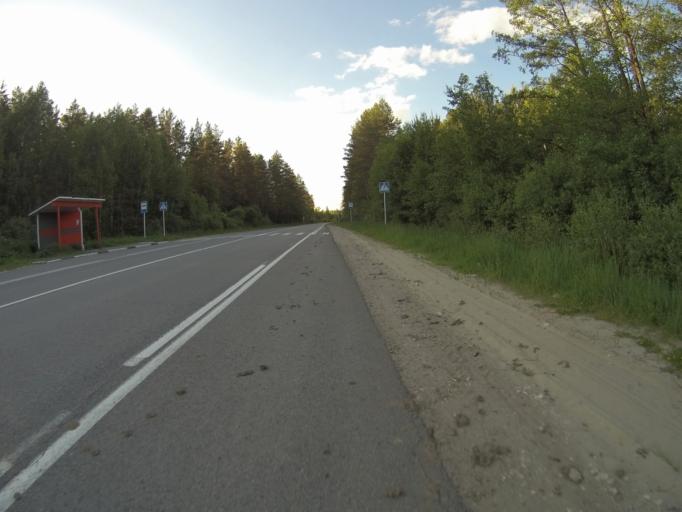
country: RU
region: Vladimir
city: Anopino
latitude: 55.8847
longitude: 40.6177
